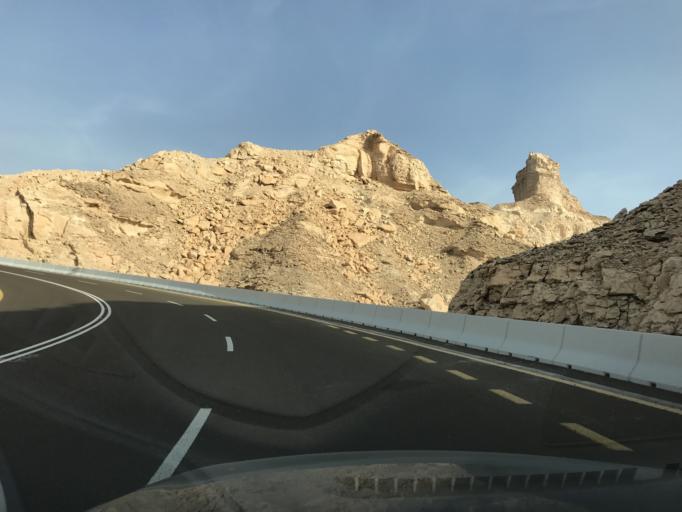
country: AE
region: Abu Dhabi
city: Al Ain
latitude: 24.1027
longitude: 55.7587
